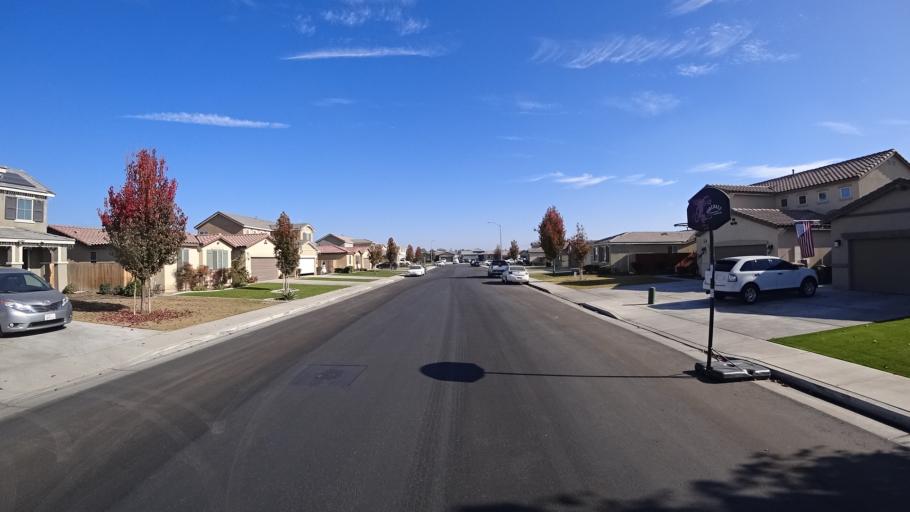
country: US
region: California
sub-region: Kern County
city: Greenfield
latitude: 35.2893
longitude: -119.0641
